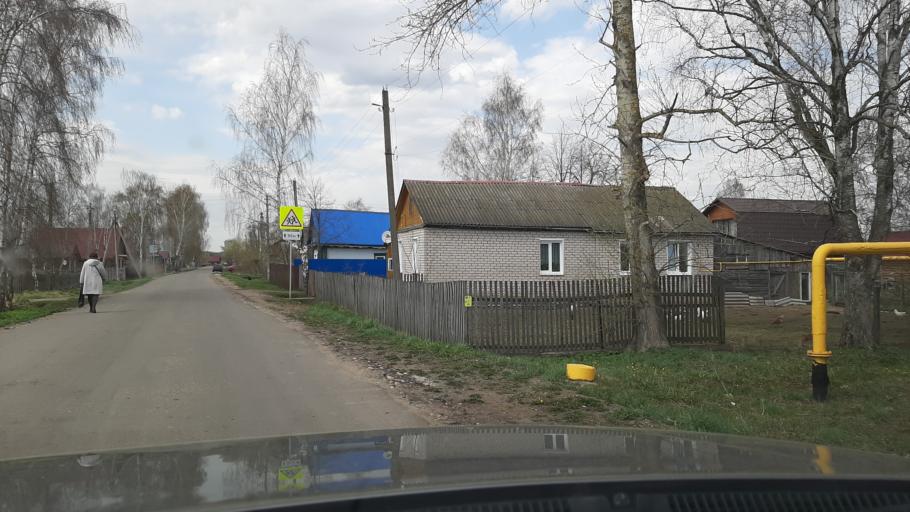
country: RU
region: Ivanovo
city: Privolzhsk
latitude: 57.3297
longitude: 41.2347
